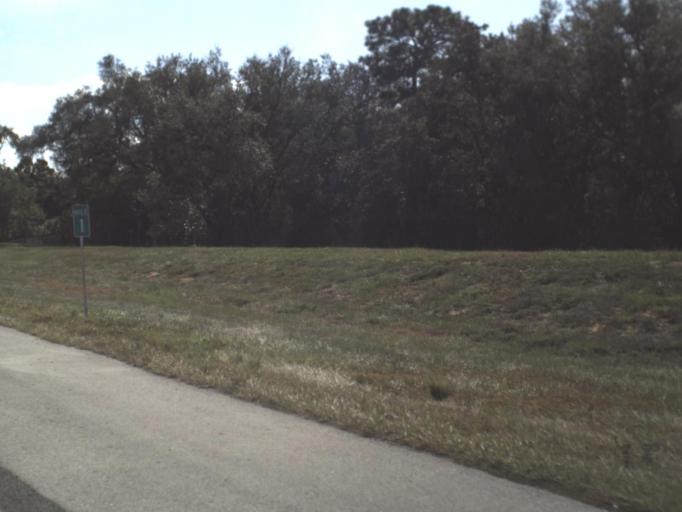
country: US
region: Florida
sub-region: Polk County
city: Loughman
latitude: 28.2877
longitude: -81.5970
